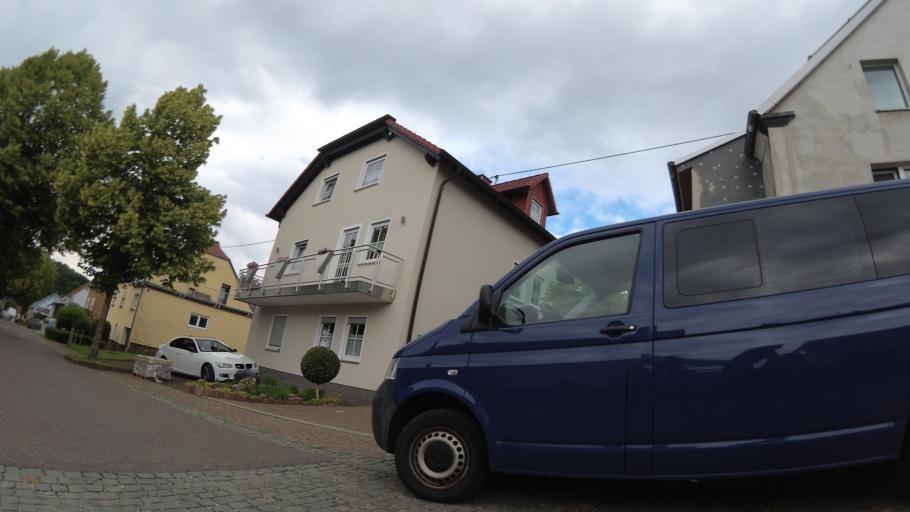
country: DE
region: Saarland
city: Tholey
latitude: 49.4953
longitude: 7.0289
